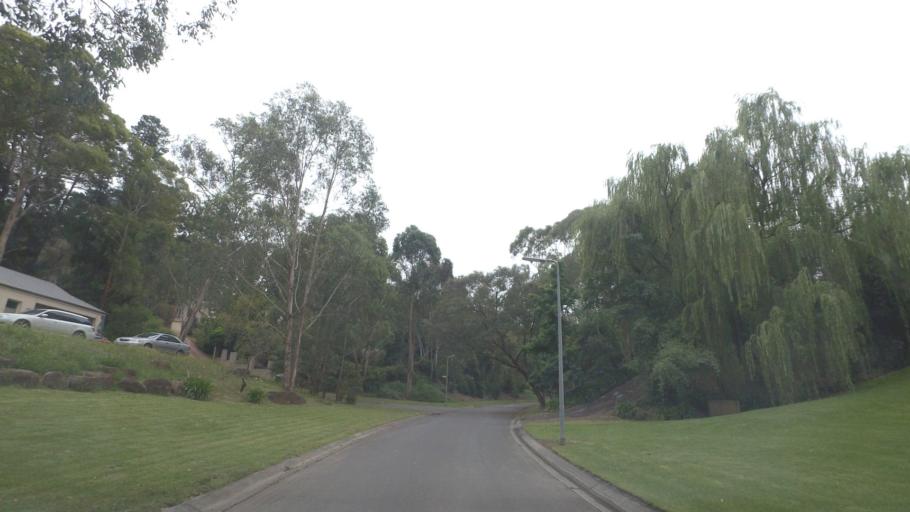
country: AU
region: Victoria
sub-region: Manningham
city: Park Orchards
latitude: -37.7892
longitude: 145.2090
